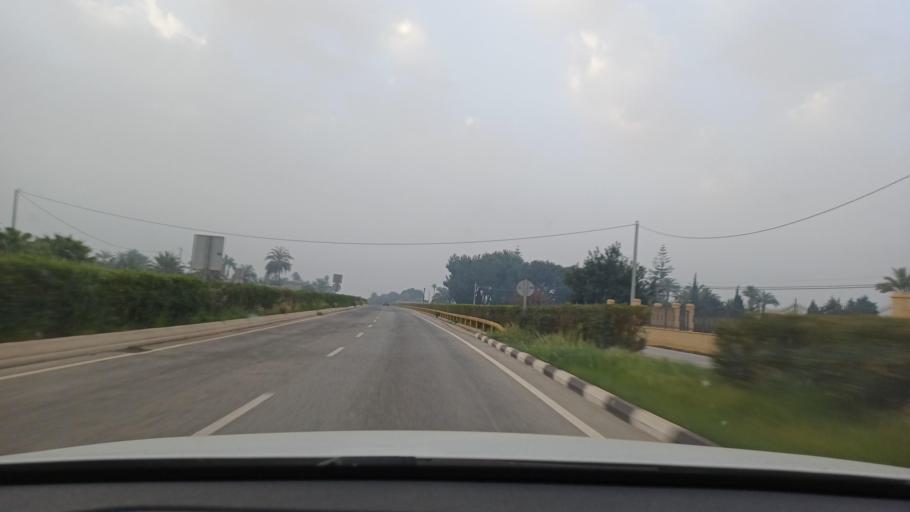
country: ES
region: Valencia
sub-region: Provincia de Alicante
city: Elche
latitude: 38.2040
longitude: -0.7001
